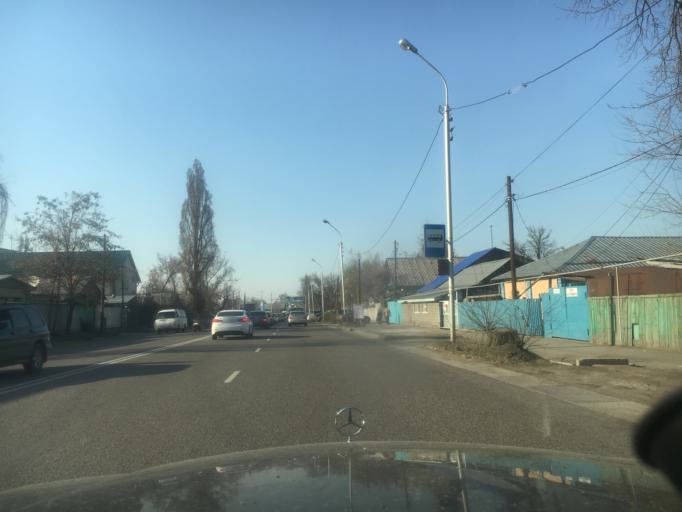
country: KZ
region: Almaty Qalasy
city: Almaty
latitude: 43.2828
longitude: 76.9389
